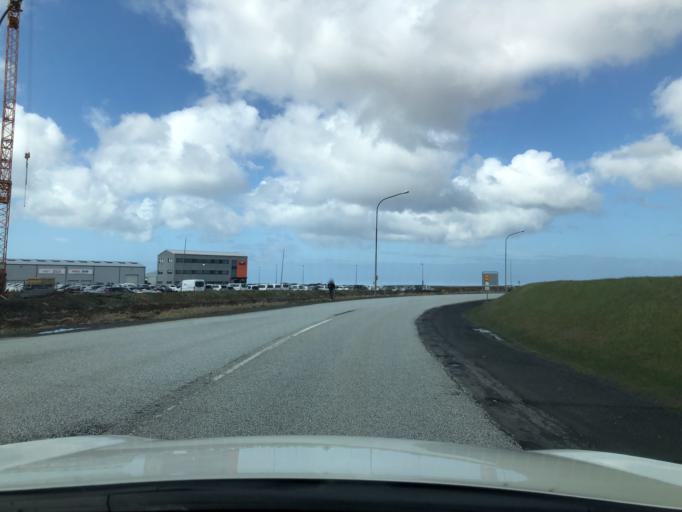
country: IS
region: Southern Peninsula
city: Reykjanesbaer
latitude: 63.9982
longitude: -22.6268
